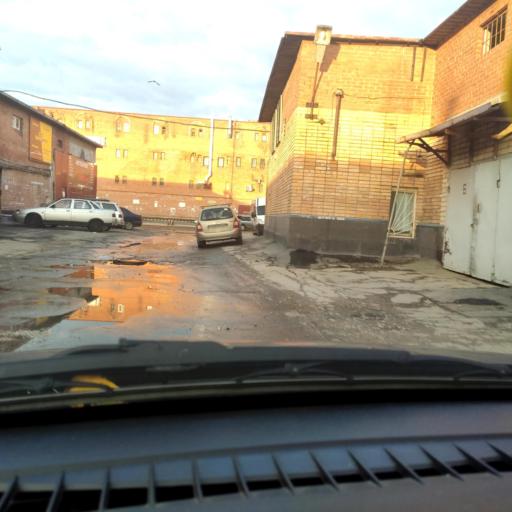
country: RU
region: Samara
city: Tol'yatti
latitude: 53.5392
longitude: 49.2909
